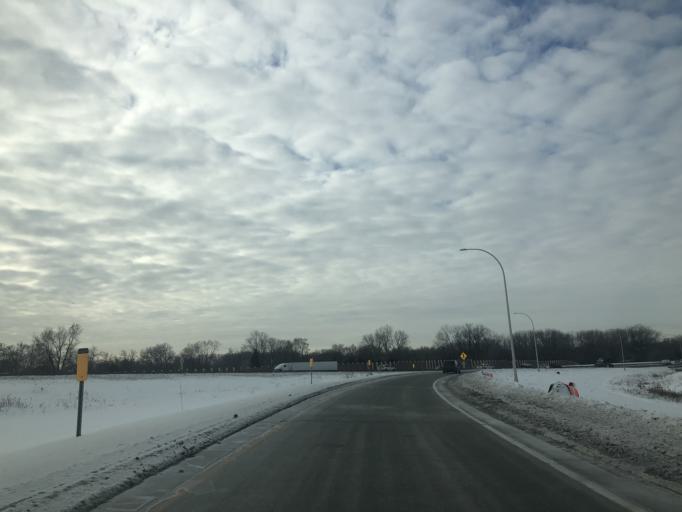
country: US
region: Minnesota
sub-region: Ramsey County
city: Mounds View
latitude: 45.1168
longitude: -93.1901
